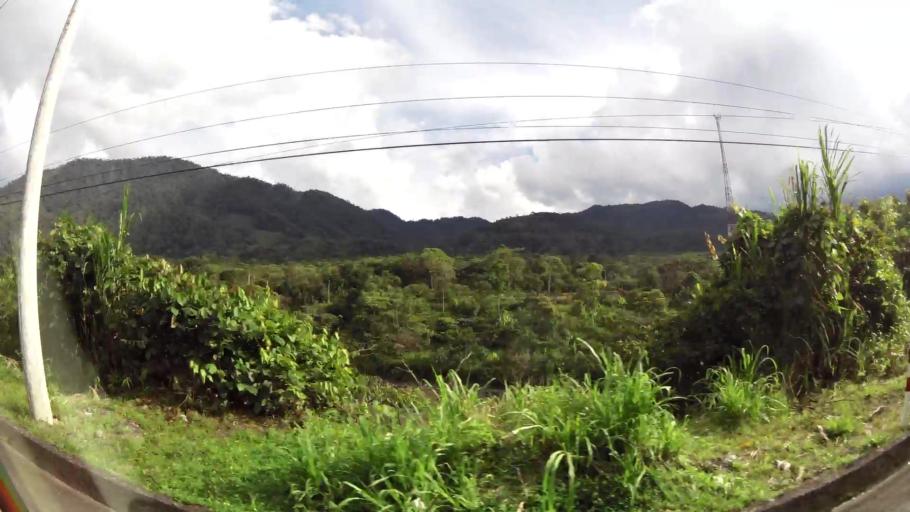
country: EC
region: Pastaza
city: Puyo
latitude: -1.4125
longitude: -78.2054
